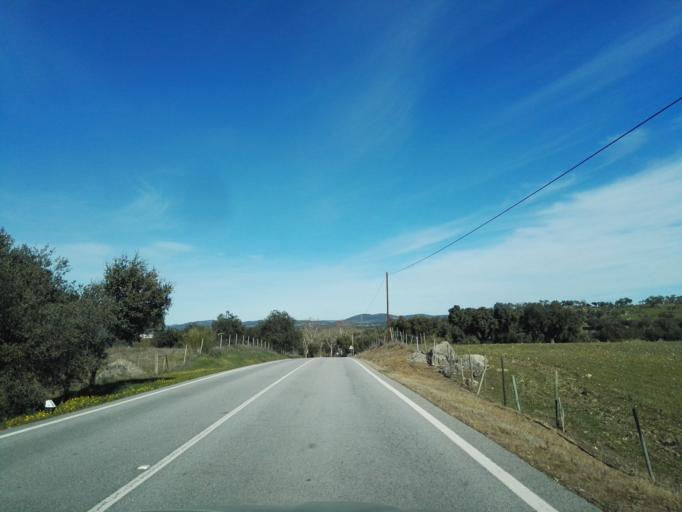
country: PT
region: Portalegre
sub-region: Arronches
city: Arronches
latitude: 39.1012
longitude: -7.2787
